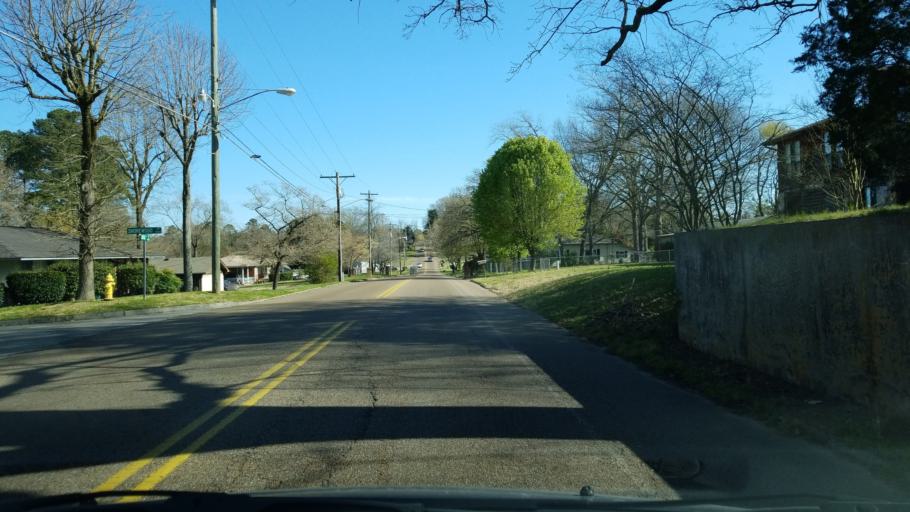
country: US
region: Tennessee
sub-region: Hamilton County
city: Harrison
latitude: 35.0826
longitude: -85.1855
